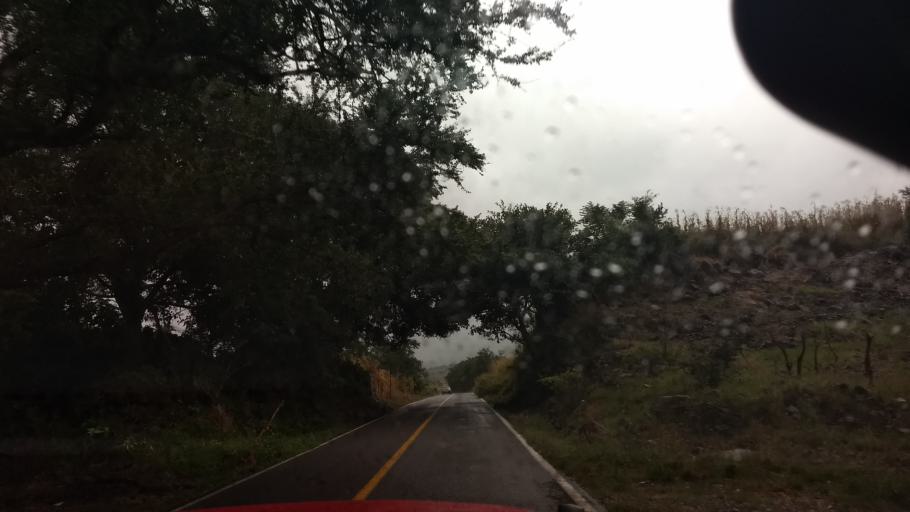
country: MX
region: Jalisco
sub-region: Tonila
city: San Marcos
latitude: 19.4397
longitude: -103.4908
